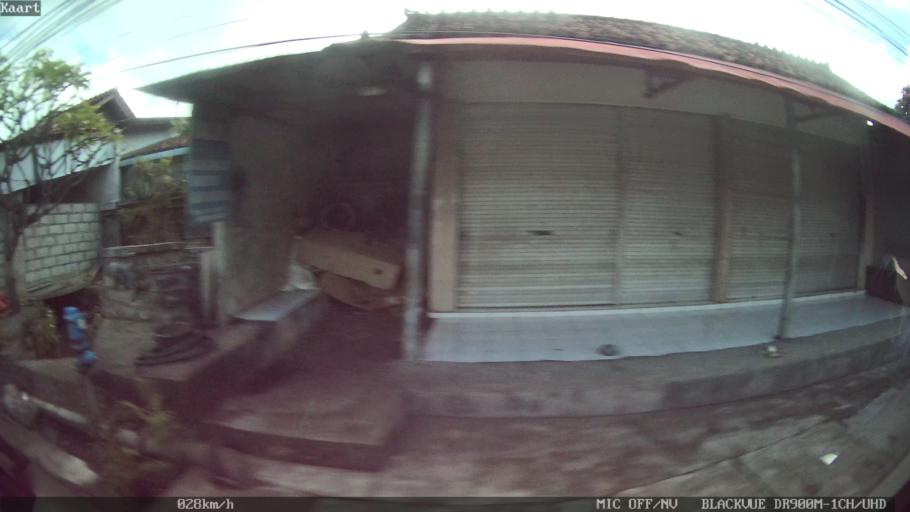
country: ID
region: Bali
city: Banjar Pasekan
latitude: -8.5988
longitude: 115.2859
